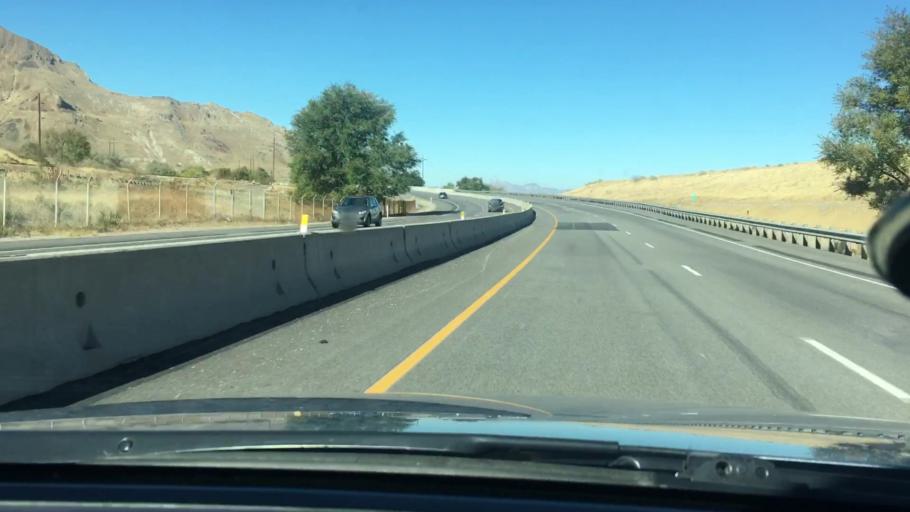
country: US
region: Utah
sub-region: Salt Lake County
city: Magna
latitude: 40.7205
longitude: -112.1505
